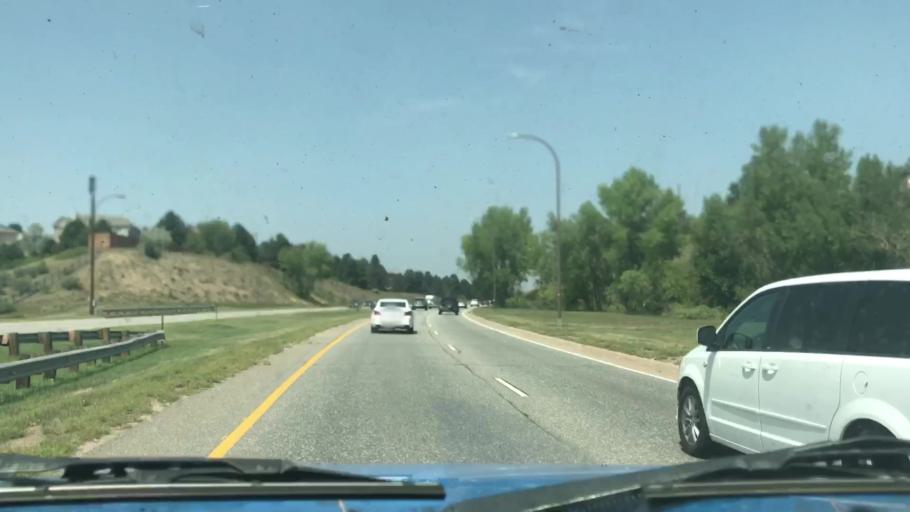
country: US
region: Colorado
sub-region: Jefferson County
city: Lakewood
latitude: 39.6741
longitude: -105.1190
